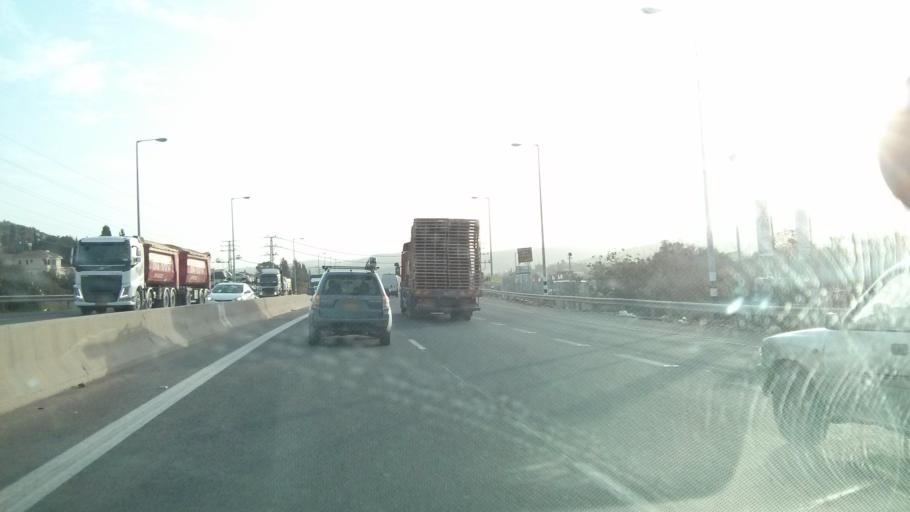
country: PS
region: West Bank
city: Barta`ah ash Sharqiyah
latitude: 32.5017
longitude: 35.0754
